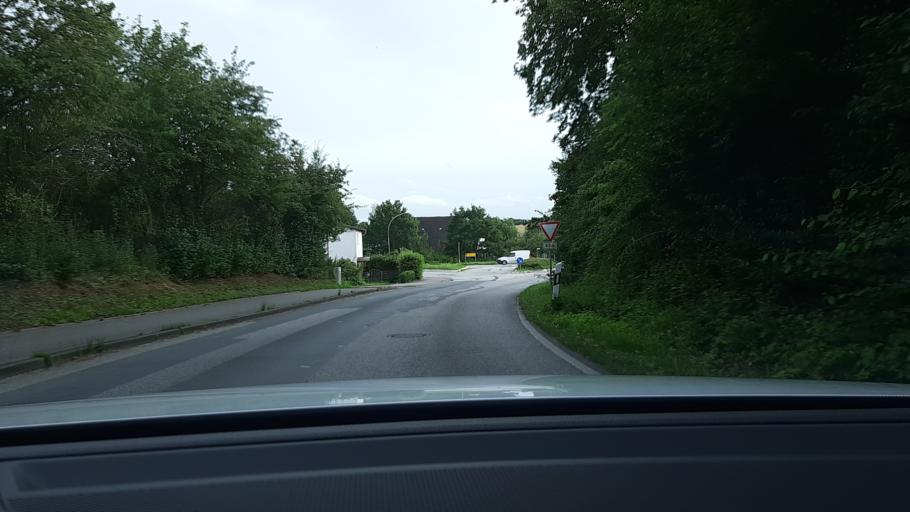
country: DE
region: Schleswig-Holstein
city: Wesenberg
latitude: 53.8378
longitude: 10.5563
